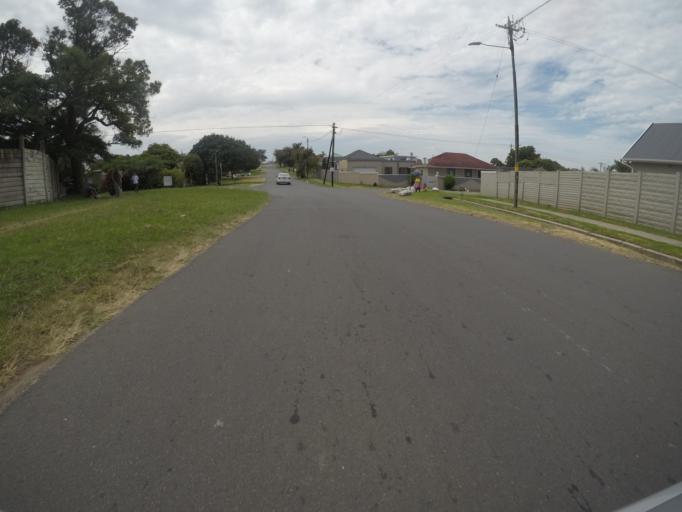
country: ZA
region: Eastern Cape
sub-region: Buffalo City Metropolitan Municipality
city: East London
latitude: -32.9743
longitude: 27.8707
